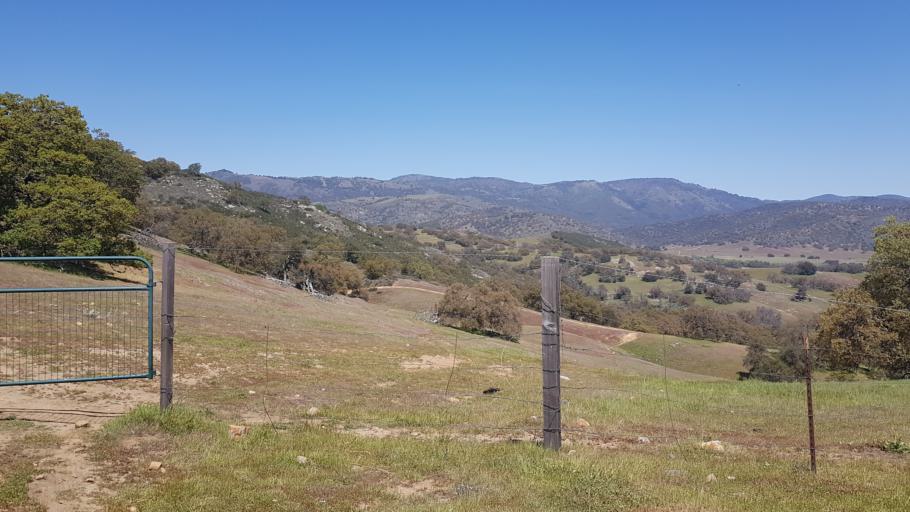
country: US
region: California
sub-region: San Diego County
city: Julian
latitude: 33.1231
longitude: -116.7087
